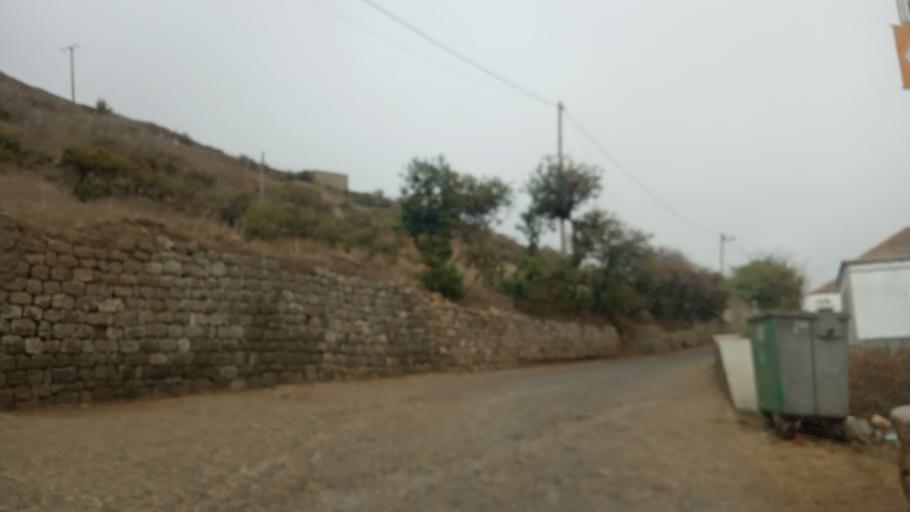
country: CV
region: Brava
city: Vila Nova Sintra
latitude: 14.8710
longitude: -24.7025
